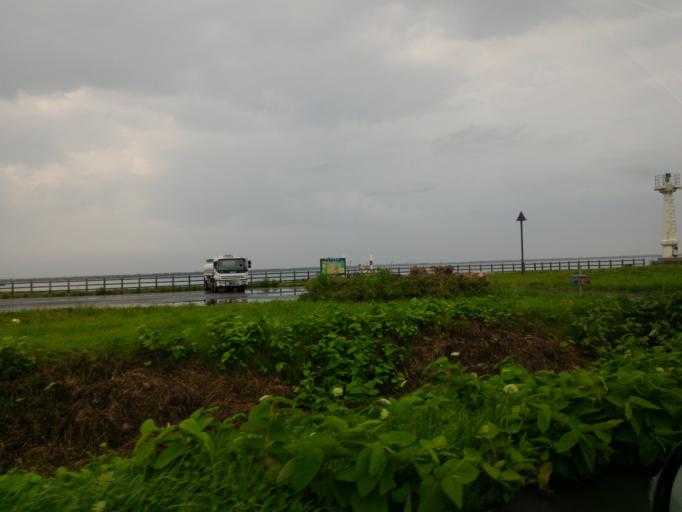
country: JP
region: Hokkaido
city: Rumoi
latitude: 43.9605
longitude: 141.6431
